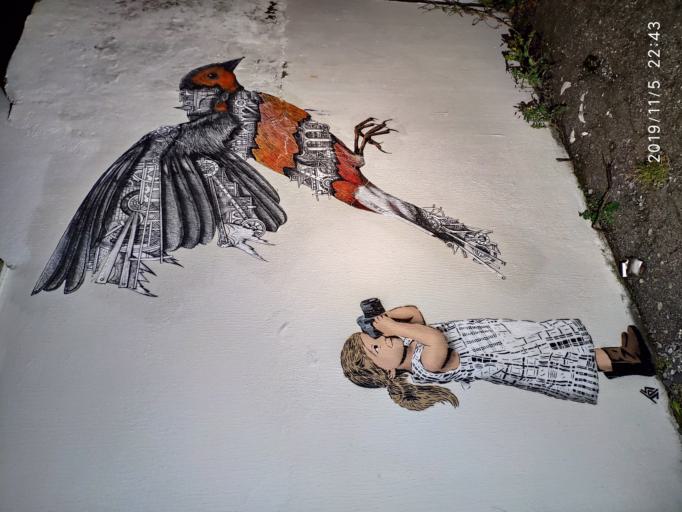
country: NO
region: Rogaland
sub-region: Stavanger
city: Stavanger
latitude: 58.9709
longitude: 5.7493
